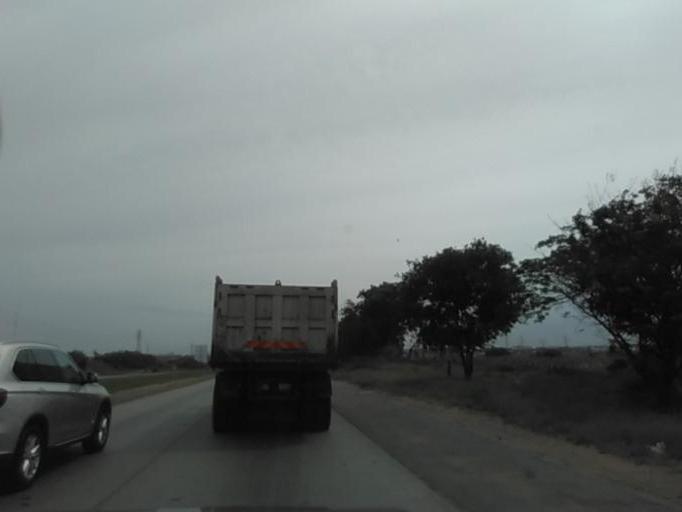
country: GH
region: Greater Accra
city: Tema
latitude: 5.6783
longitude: -0.0360
